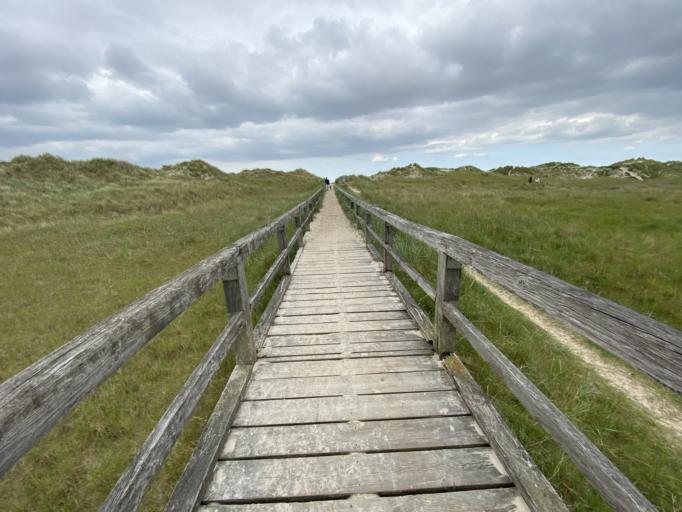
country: DE
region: Schleswig-Holstein
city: Sankt Peter-Ording
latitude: 54.3414
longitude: 8.6051
